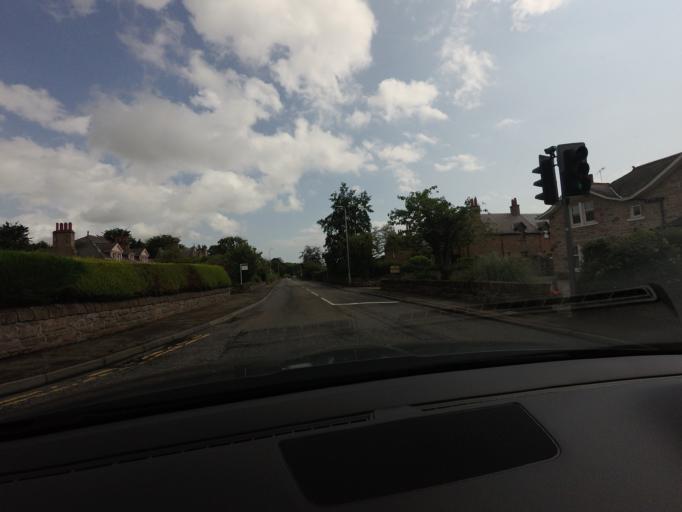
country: GB
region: Scotland
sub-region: Highland
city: Dingwall
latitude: 57.6010
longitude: -4.4281
